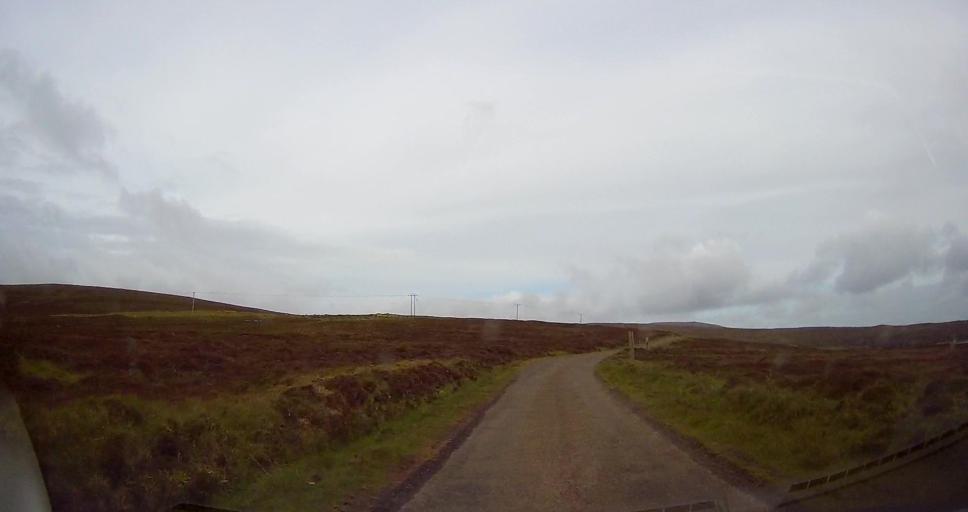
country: GB
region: Scotland
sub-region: Orkney Islands
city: Stromness
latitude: 58.8541
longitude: -3.2099
